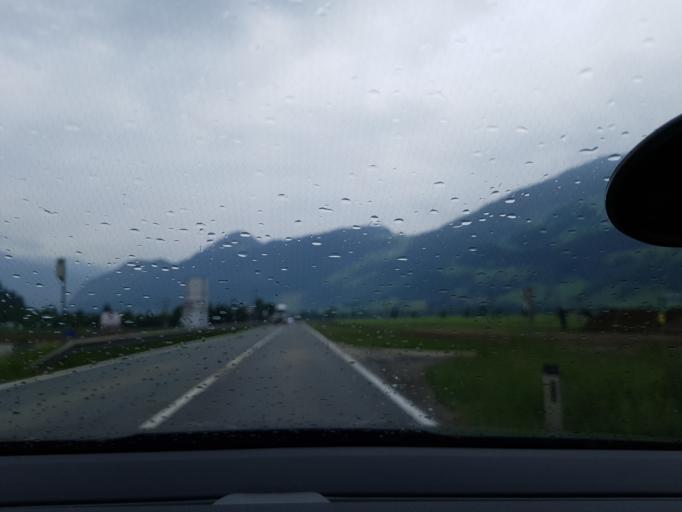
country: AT
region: Tyrol
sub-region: Politischer Bezirk Schwaz
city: Fugen
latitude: 47.3551
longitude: 11.8518
